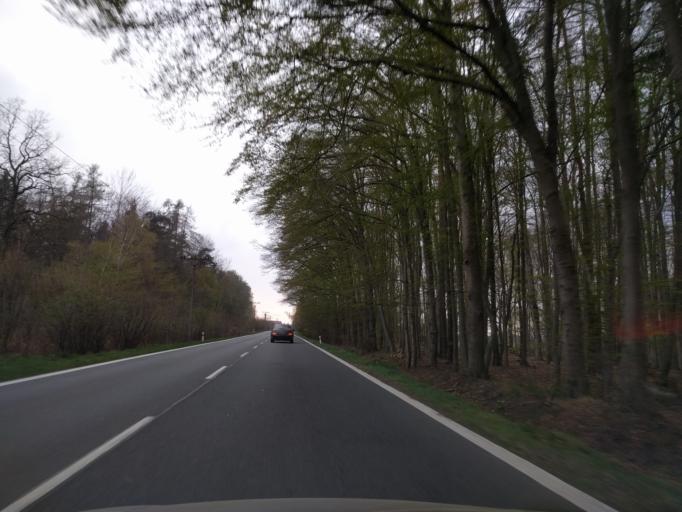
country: CZ
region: Central Bohemia
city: Mukarov
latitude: 49.9898
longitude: 14.7978
